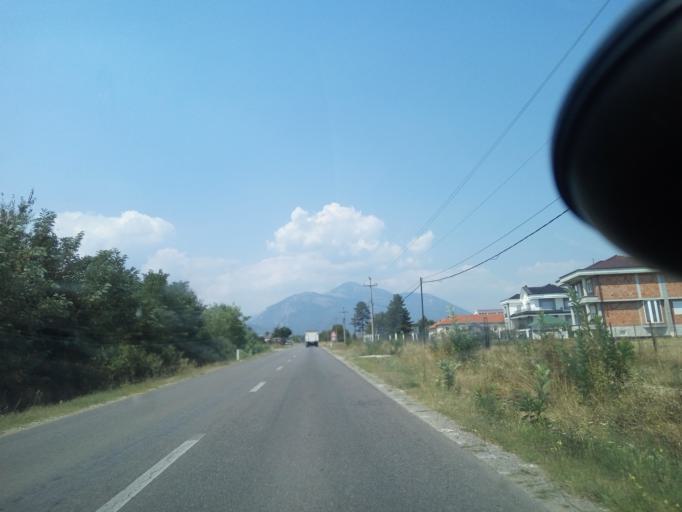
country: XK
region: Gjakova
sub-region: Komuna e Decanit
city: Prilep
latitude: 42.4843
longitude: 20.3296
